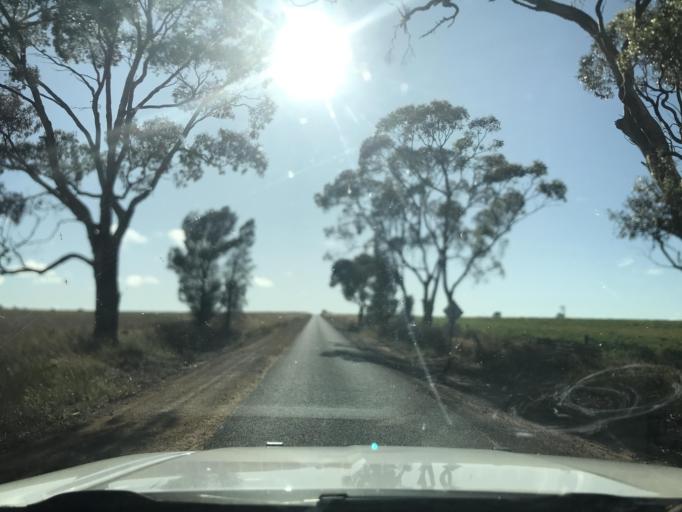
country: AU
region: Victoria
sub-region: Horsham
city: Horsham
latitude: -36.6953
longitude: 141.5767
